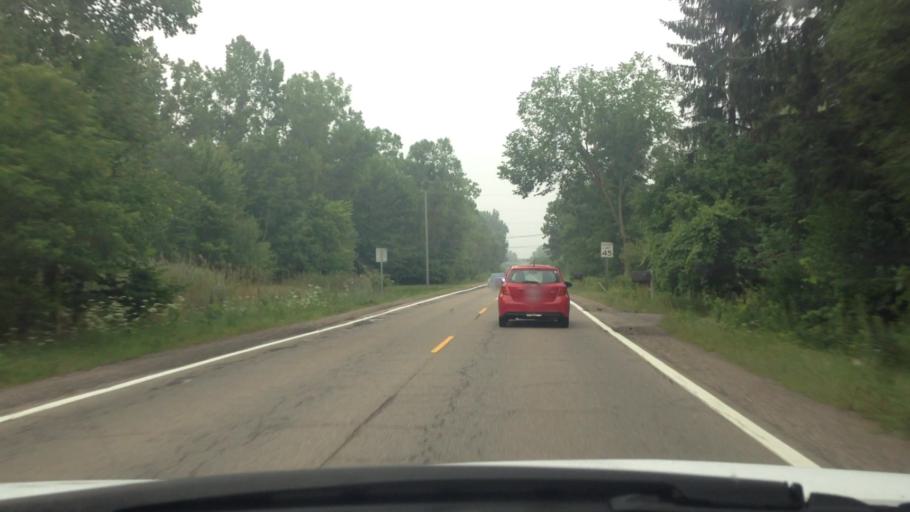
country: US
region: Michigan
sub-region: Oakland County
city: Clarkston
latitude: 42.7283
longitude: -83.3497
